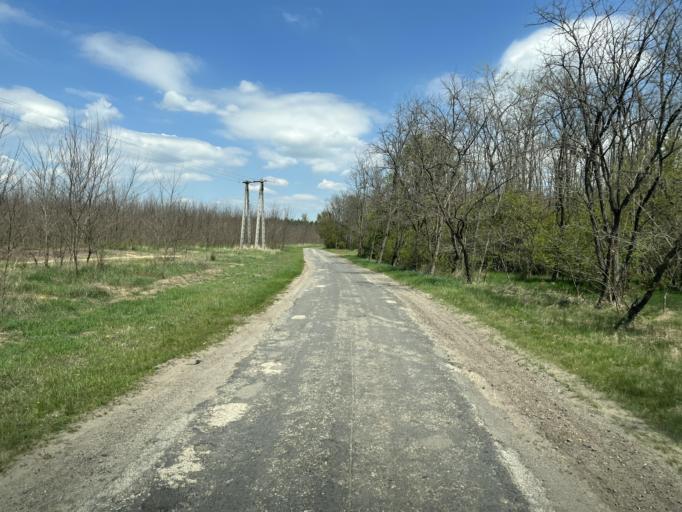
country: HU
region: Pest
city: Inarcs
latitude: 47.2699
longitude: 19.3546
